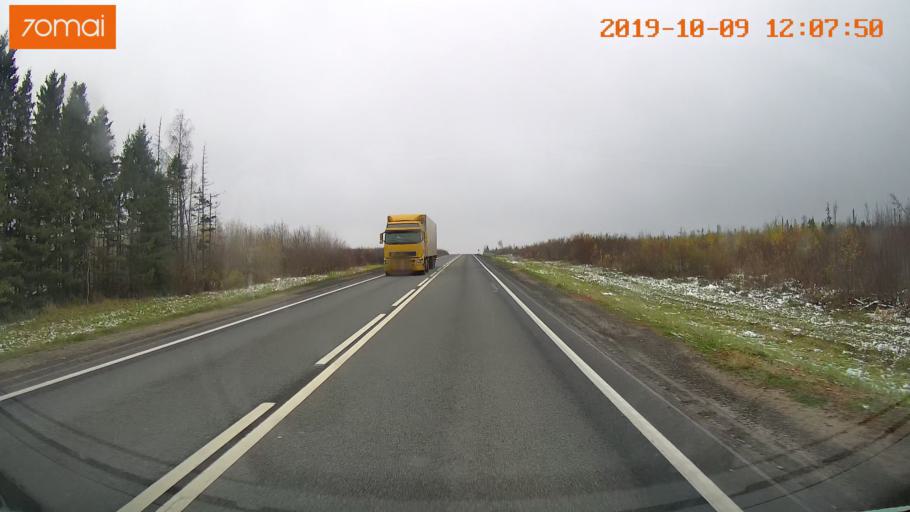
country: RU
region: Jaroslavl
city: Prechistoye
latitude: 58.5945
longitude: 40.3440
